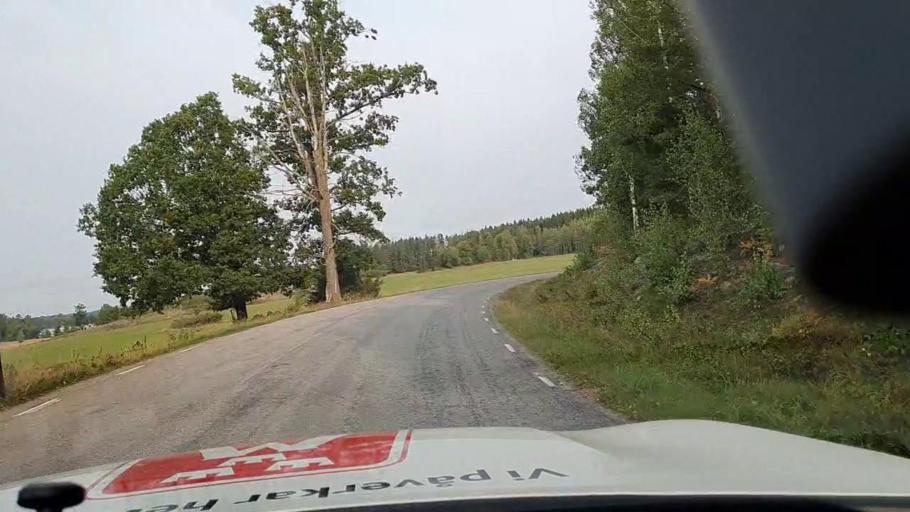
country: SE
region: Soedermanland
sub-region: Nykopings Kommun
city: Stigtomta
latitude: 58.9732
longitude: 16.8983
